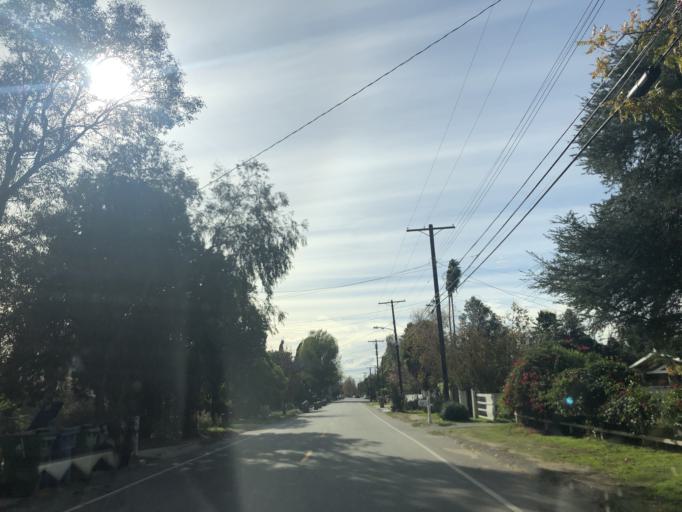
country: US
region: California
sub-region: Los Angeles County
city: San Fernando
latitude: 34.2795
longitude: -118.3748
